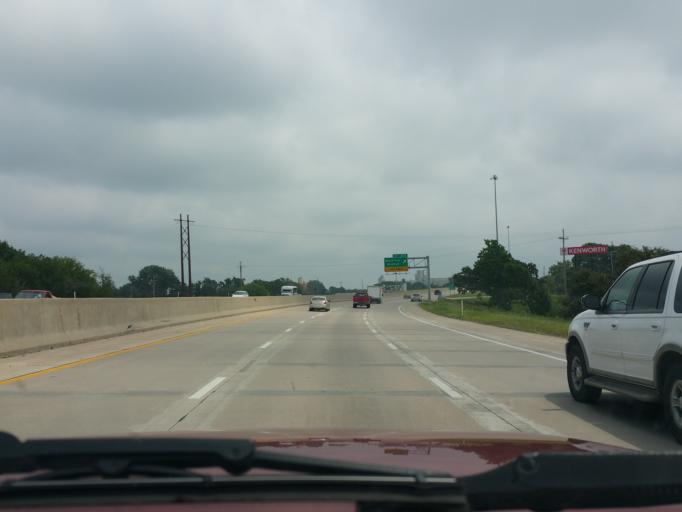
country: US
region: Kansas
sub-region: Shawnee County
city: Topeka
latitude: 39.0696
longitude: -95.7114
